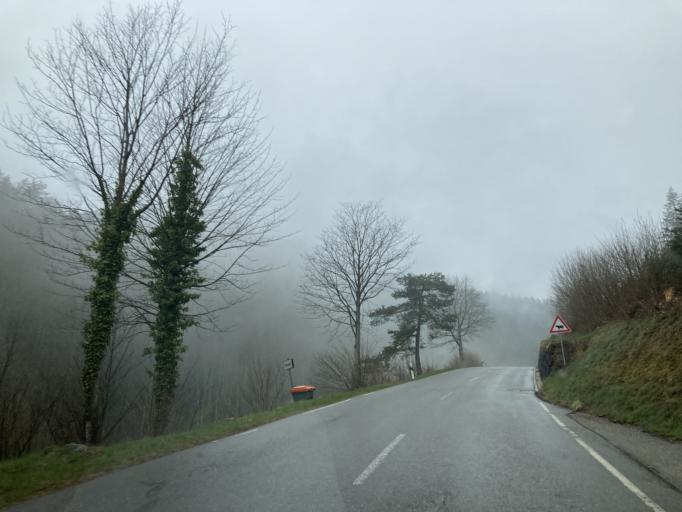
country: DE
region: Baden-Wuerttemberg
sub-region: Freiburg Region
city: Hornberg
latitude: 48.2295
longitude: 8.2686
